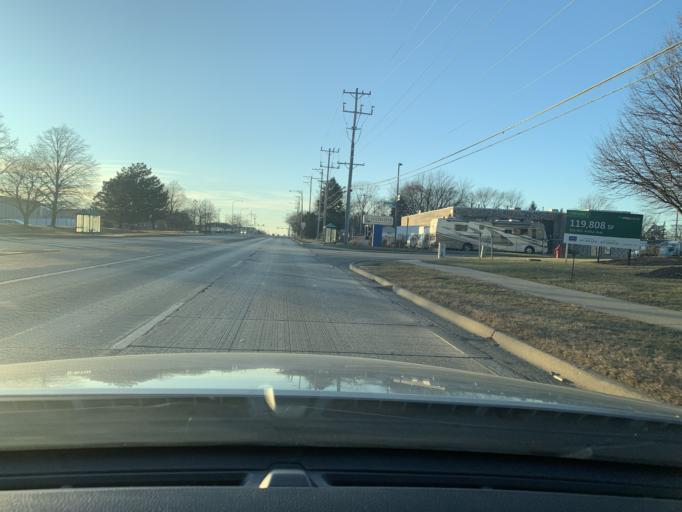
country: US
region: Illinois
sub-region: Cook County
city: Elk Grove Village
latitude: 41.9930
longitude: -87.9750
